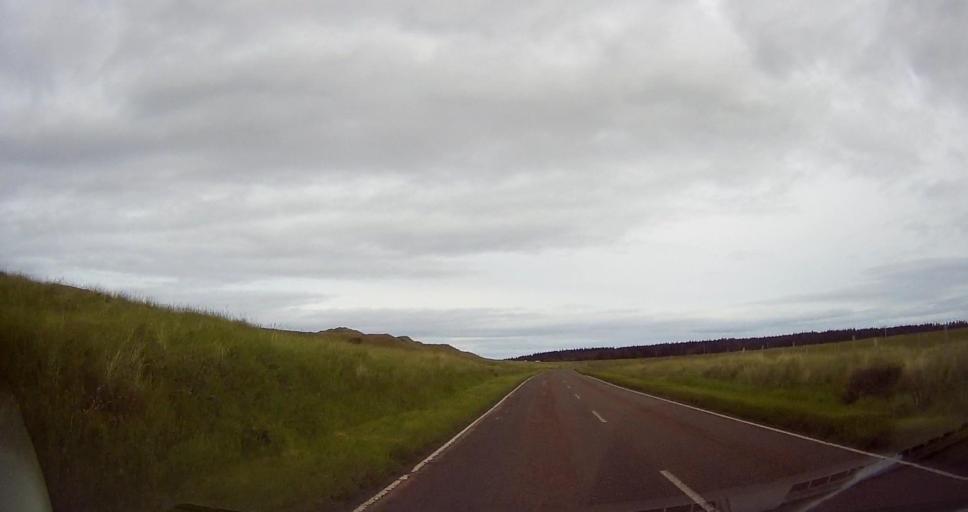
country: GB
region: Scotland
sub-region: Highland
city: Thurso
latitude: 58.6027
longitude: -3.3484
